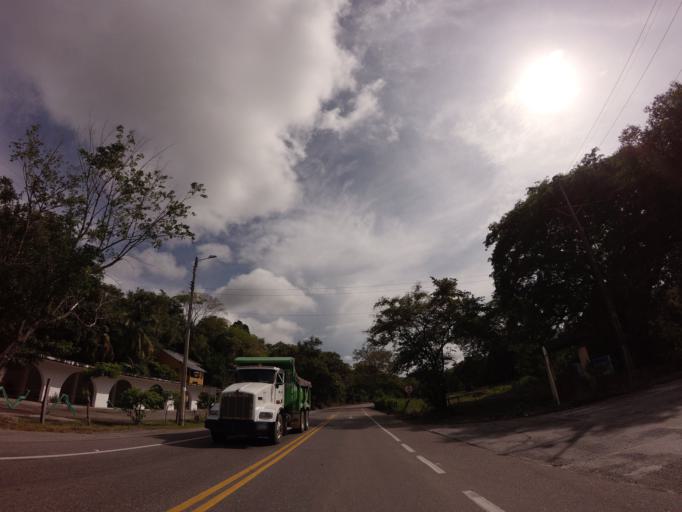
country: CO
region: Tolima
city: Honda
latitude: 5.2146
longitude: -74.7382
